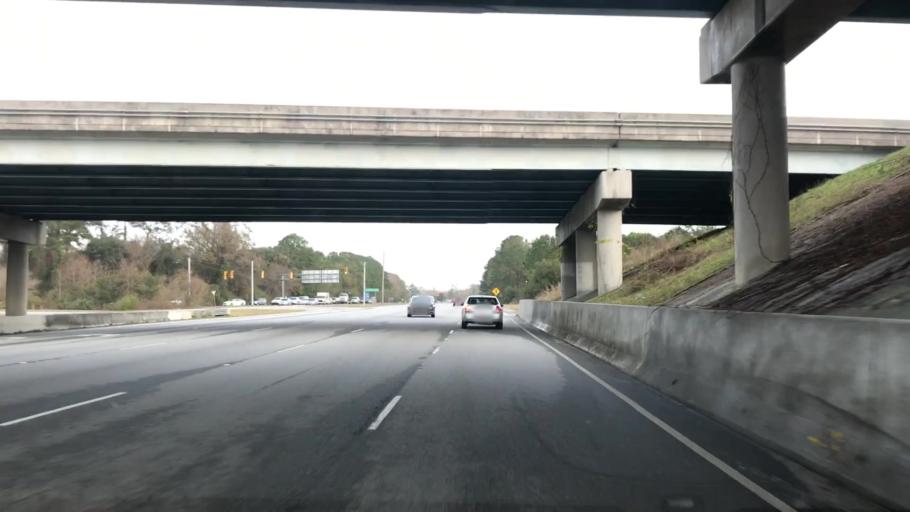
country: US
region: South Carolina
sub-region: Charleston County
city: Shell Point
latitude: 32.8095
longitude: -80.0368
